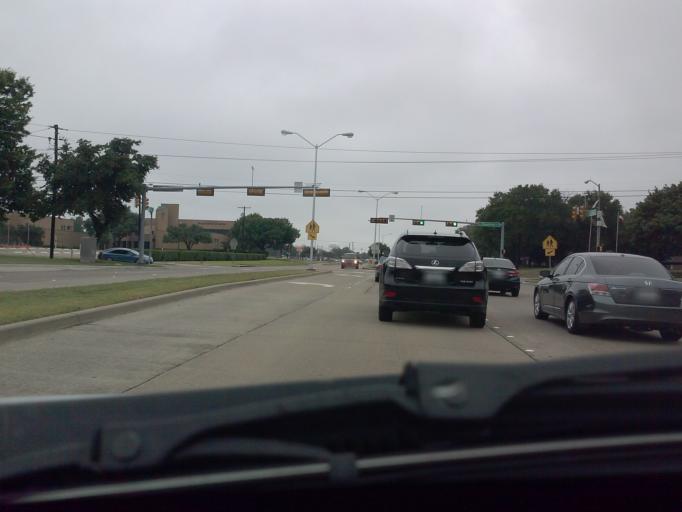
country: US
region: Texas
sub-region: Collin County
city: Plano
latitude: 33.0574
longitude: -96.7458
